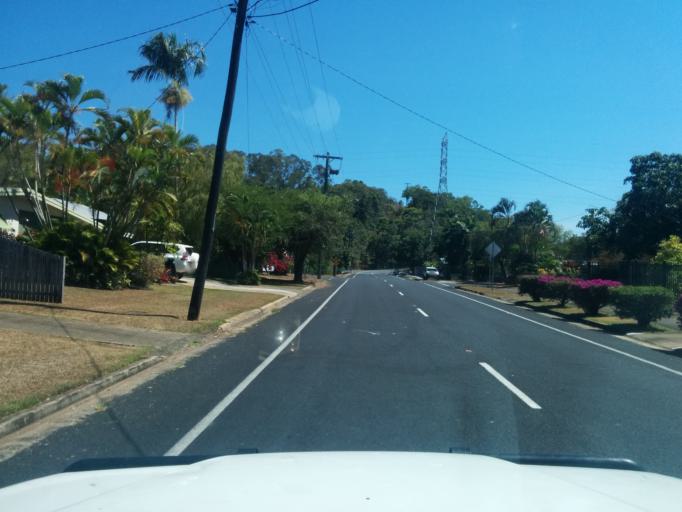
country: AU
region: Queensland
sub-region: Cairns
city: Woree
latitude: -16.9566
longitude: 145.7363
